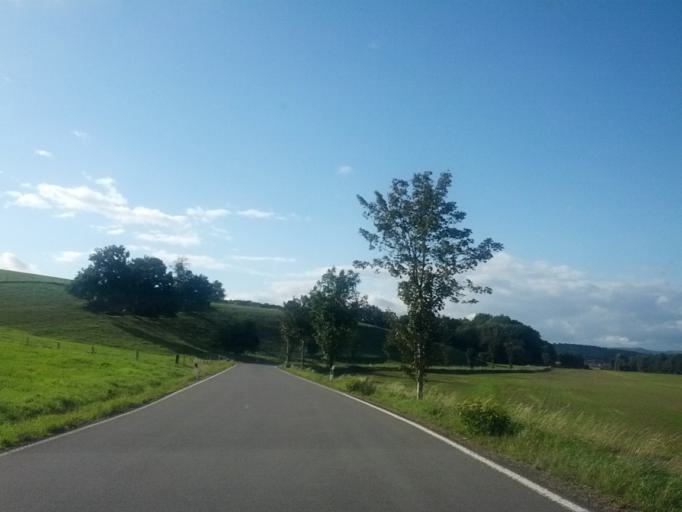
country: DE
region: Thuringia
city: Lauchroden
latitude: 50.9525
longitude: 10.1722
